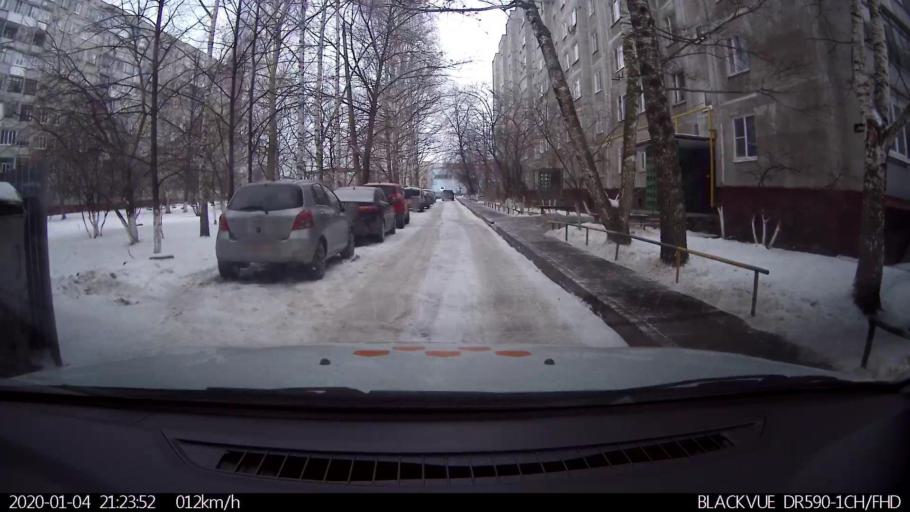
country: RU
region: Nizjnij Novgorod
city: Burevestnik
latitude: 56.2196
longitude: 43.8341
